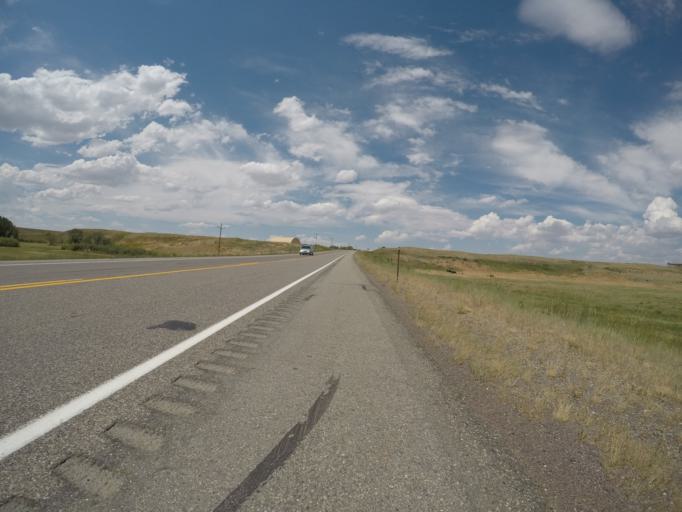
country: US
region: Wyoming
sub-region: Albany County
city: Laramie
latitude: 41.7335
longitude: -105.9717
